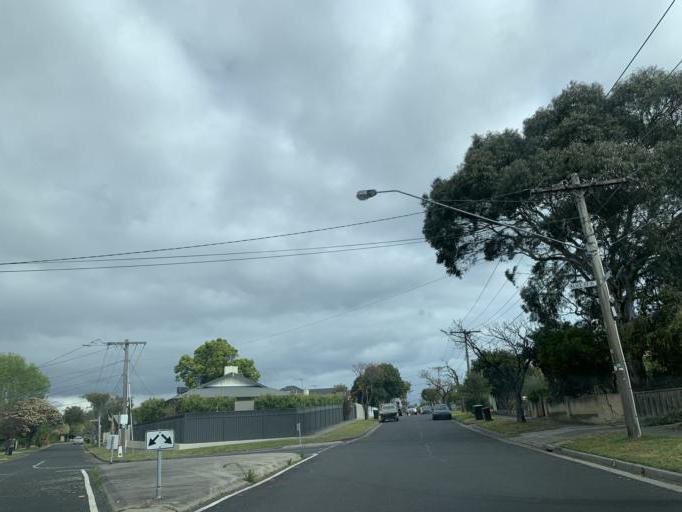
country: AU
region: Victoria
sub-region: Kingston
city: Mentone
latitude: -37.9727
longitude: 145.0785
